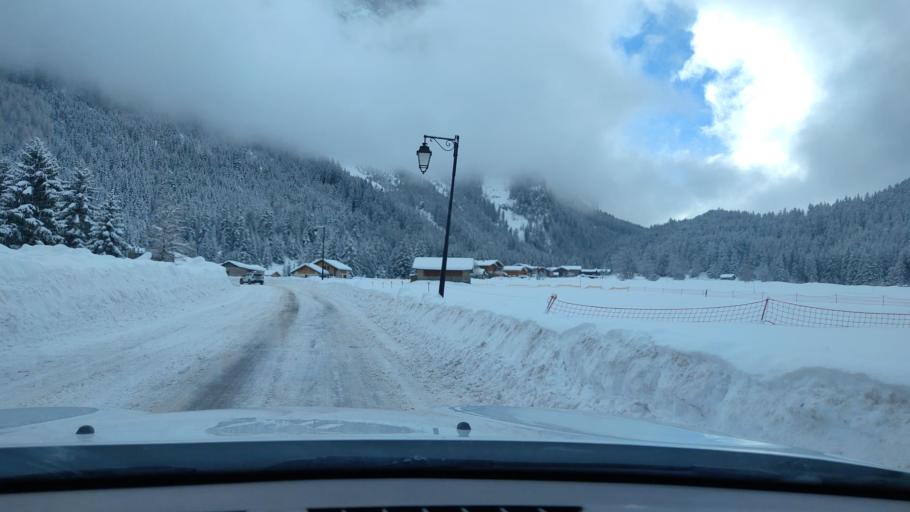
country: FR
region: Rhone-Alpes
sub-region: Departement de la Savoie
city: Courchevel
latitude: 45.3797
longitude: 6.7210
